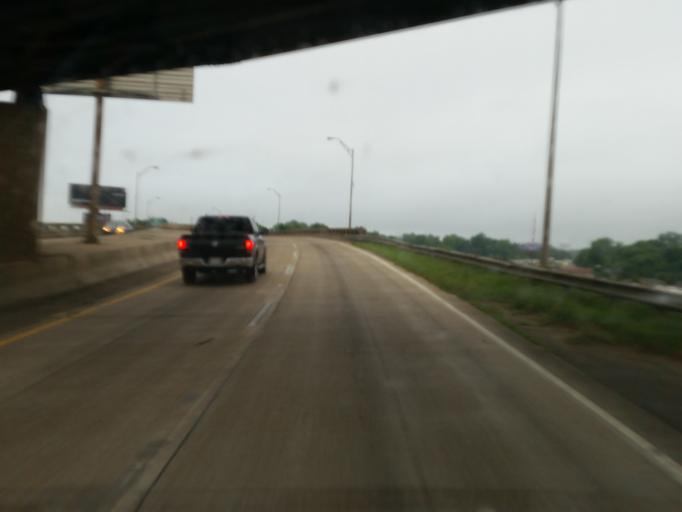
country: US
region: Louisiana
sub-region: Bossier Parish
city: Bossier City
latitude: 32.5131
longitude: -93.7164
